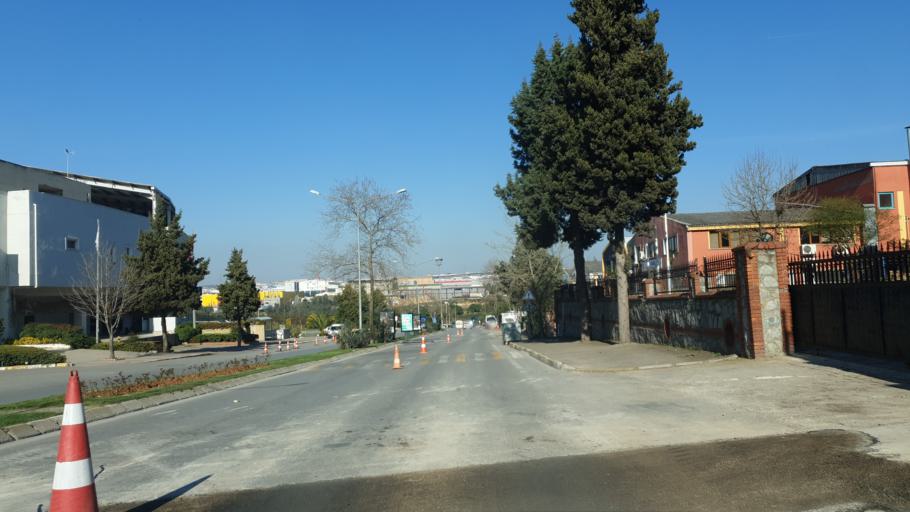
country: TR
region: Istanbul
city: Icmeler
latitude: 40.8788
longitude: 29.3521
